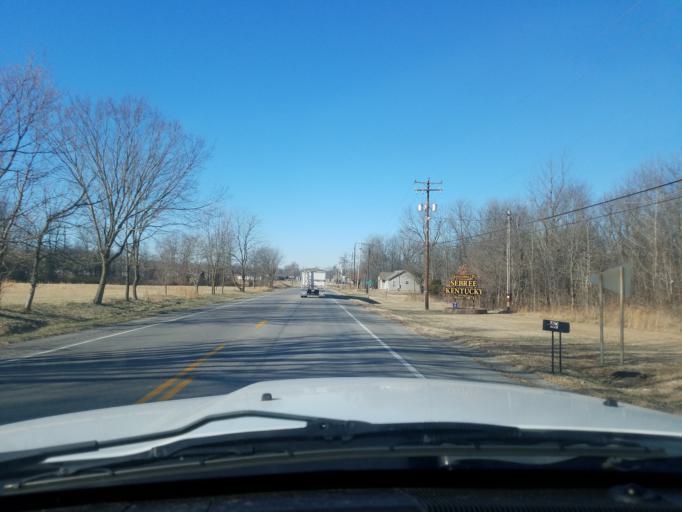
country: US
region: Kentucky
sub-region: Webster County
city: Sebree
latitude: 37.6092
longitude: -87.5215
